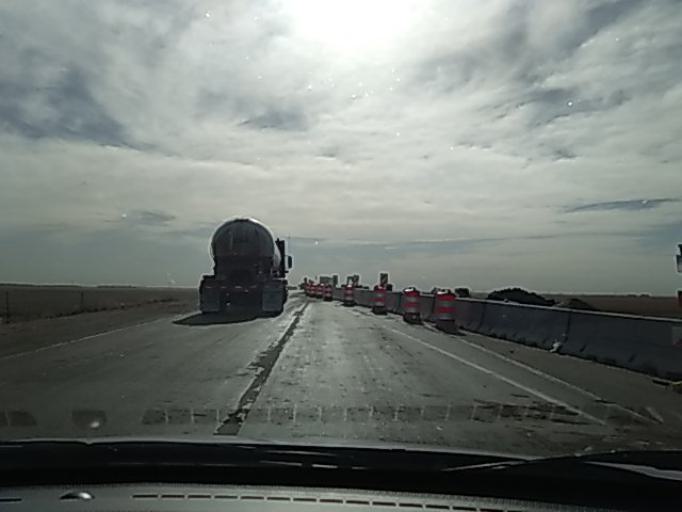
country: US
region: Nebraska
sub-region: Clay County
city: Clay Center
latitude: 40.4041
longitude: -98.0517
